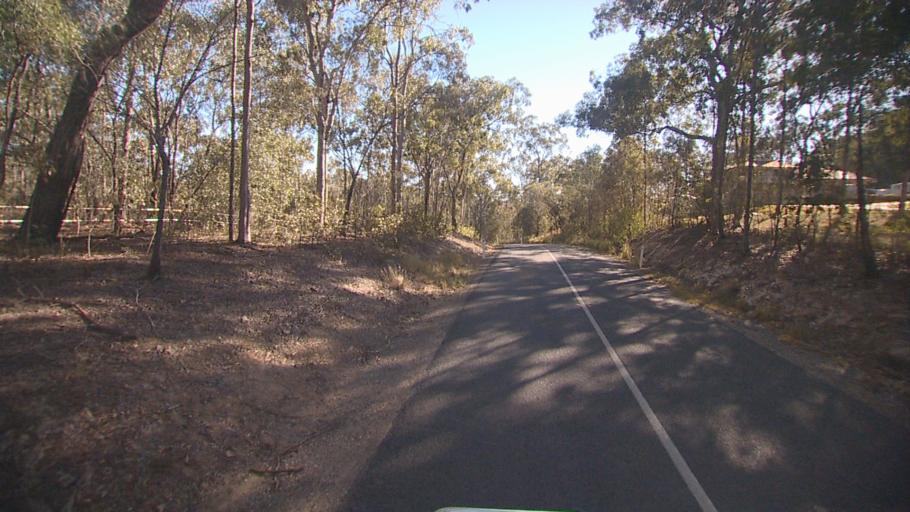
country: AU
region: Queensland
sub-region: Logan
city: Windaroo
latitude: -27.8172
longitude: 153.1687
